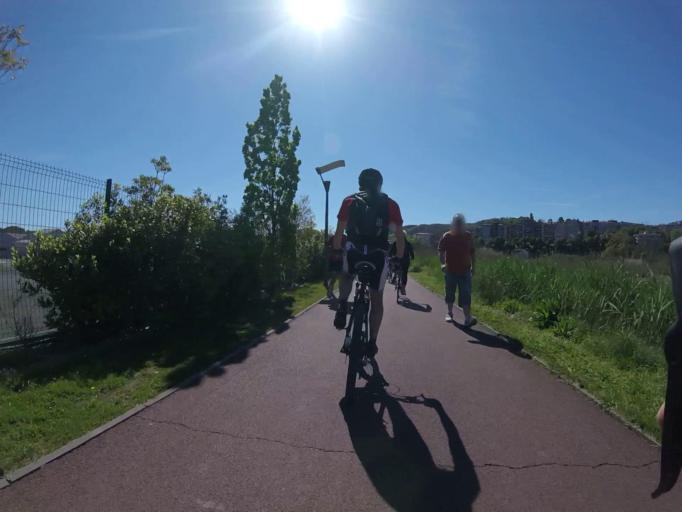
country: ES
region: Basque Country
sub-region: Provincia de Guipuzcoa
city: Irun
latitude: 43.3443
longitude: -1.7756
